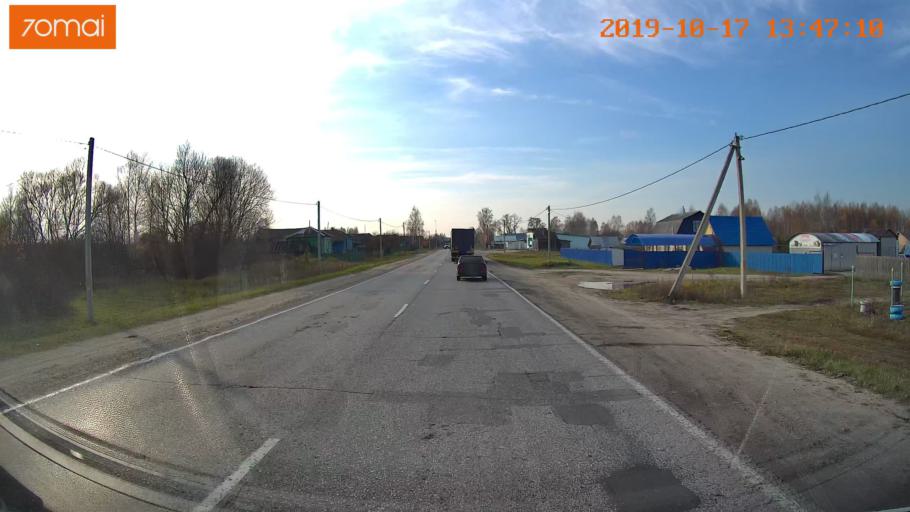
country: RU
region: Rjazan
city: Tuma
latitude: 55.1466
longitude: 40.4760
